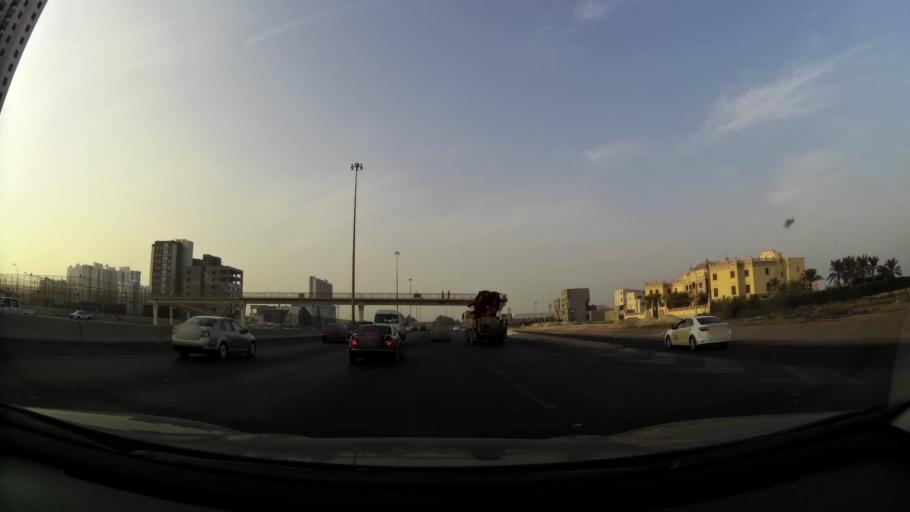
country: KW
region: Mubarak al Kabir
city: Sabah as Salim
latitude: 29.2613
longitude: 48.0875
